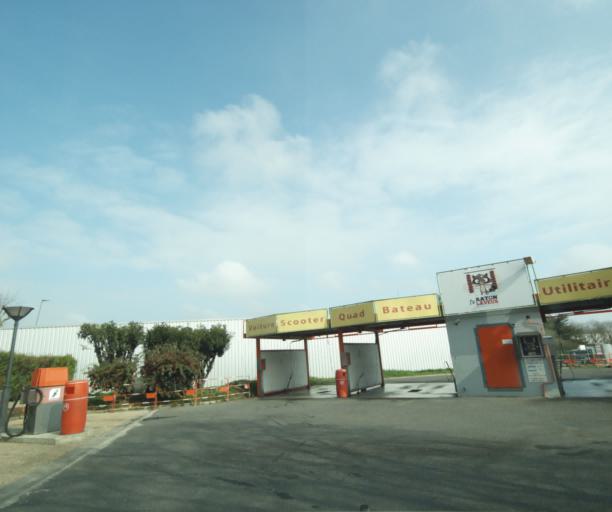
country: FR
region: Ile-de-France
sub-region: Departement du Val-d'Oise
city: Vaureal
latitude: 49.0535
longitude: 2.0236
